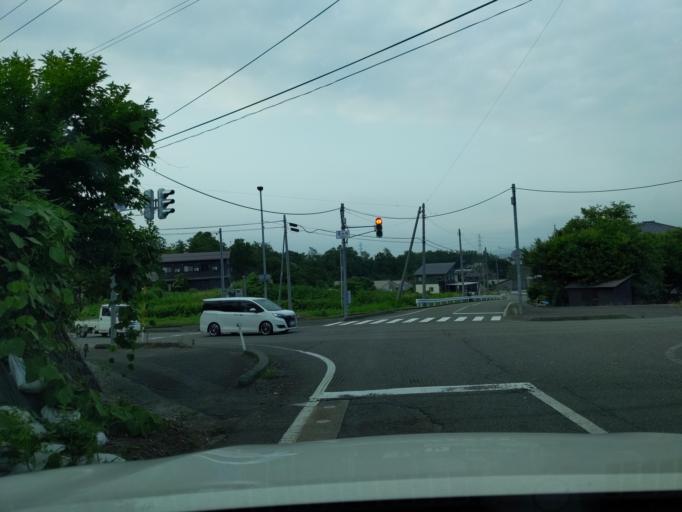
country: JP
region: Niigata
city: Kashiwazaki
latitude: 37.3976
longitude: 138.5958
